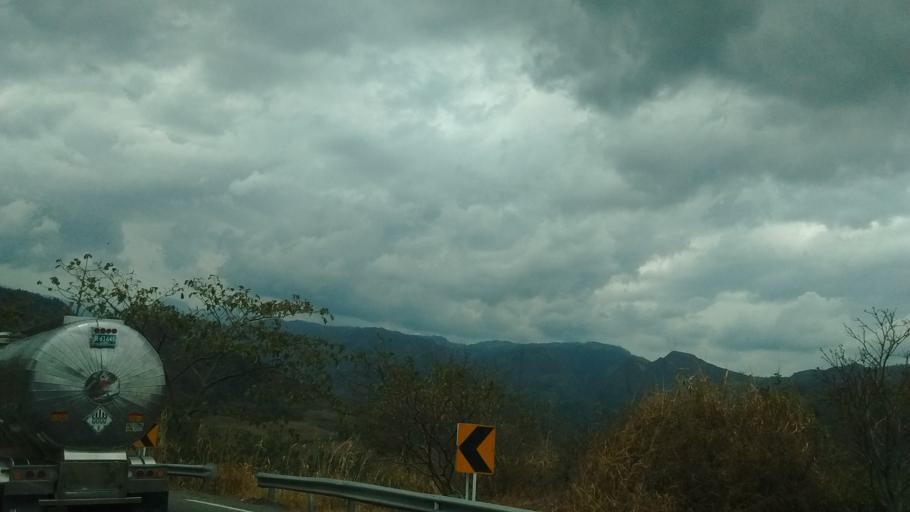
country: CO
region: Cauca
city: Rosas
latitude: 2.2919
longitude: -76.7101
